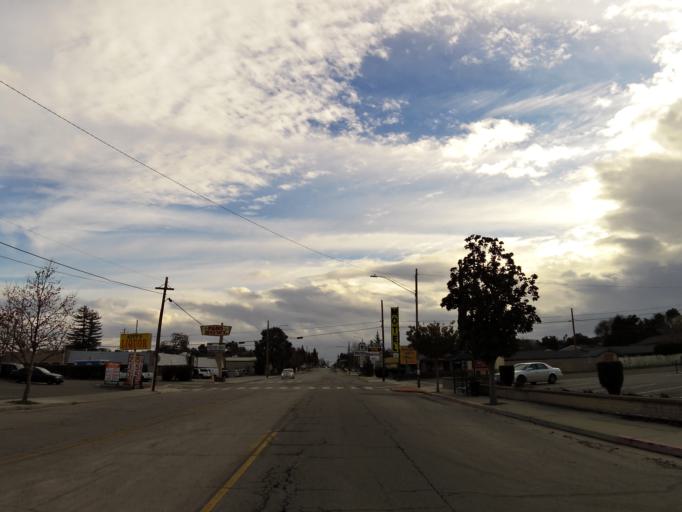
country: US
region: California
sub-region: San Luis Obispo County
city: Paso Robles
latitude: 35.6438
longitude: -120.6929
